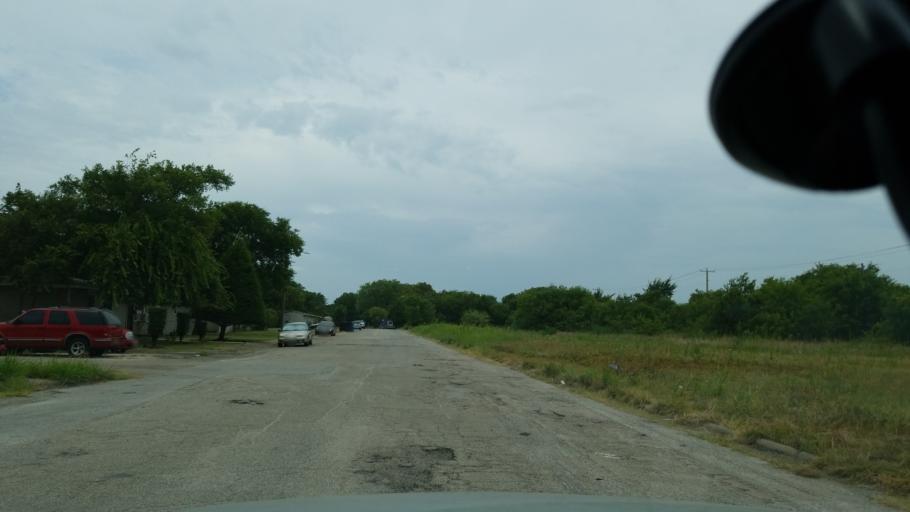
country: US
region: Texas
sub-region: Dallas County
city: Grand Prairie
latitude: 32.7377
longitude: -96.9850
